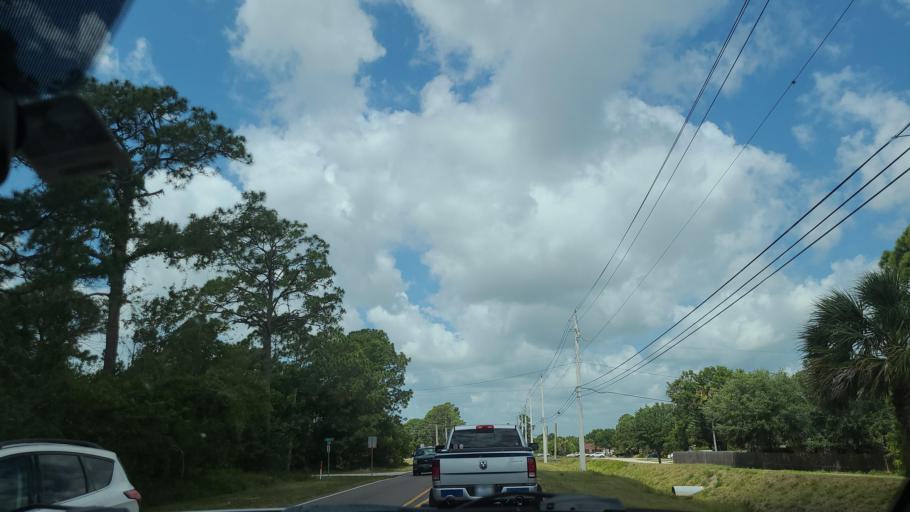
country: US
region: Florida
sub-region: Brevard County
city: June Park
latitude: 27.9991
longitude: -80.6947
